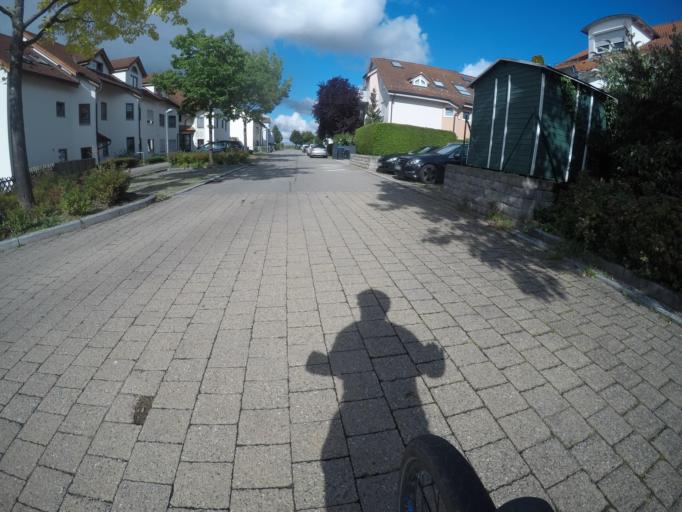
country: DE
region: Baden-Wuerttemberg
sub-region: Regierungsbezirk Stuttgart
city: Magstadt
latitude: 48.6957
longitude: 8.9584
